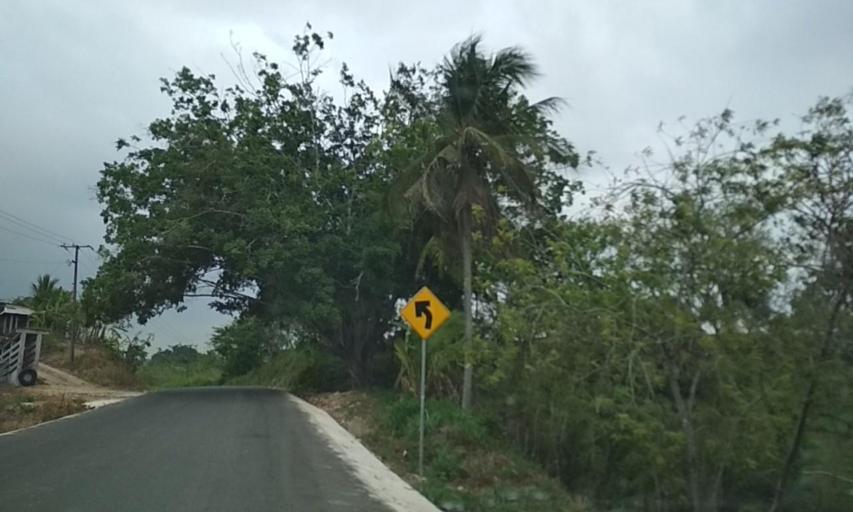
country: MX
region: Tabasco
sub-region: Huimanguillo
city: Francisco Rueda
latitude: 17.7298
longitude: -94.1021
